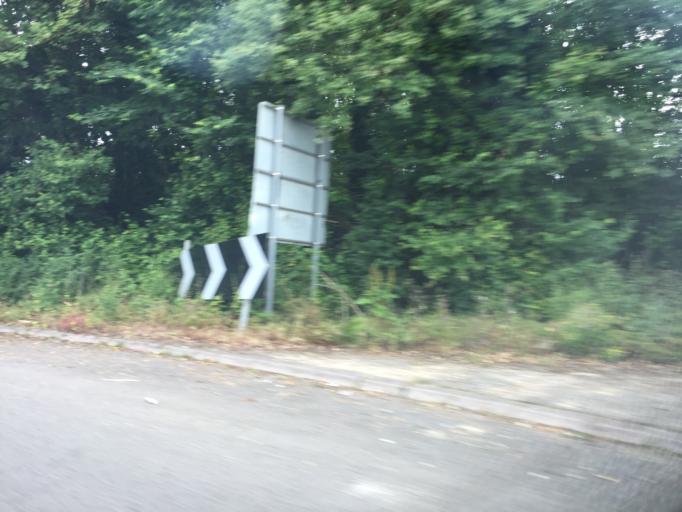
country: GB
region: England
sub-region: Borough of Swindon
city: Broad Blunsdon
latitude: 51.5976
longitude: -1.7702
